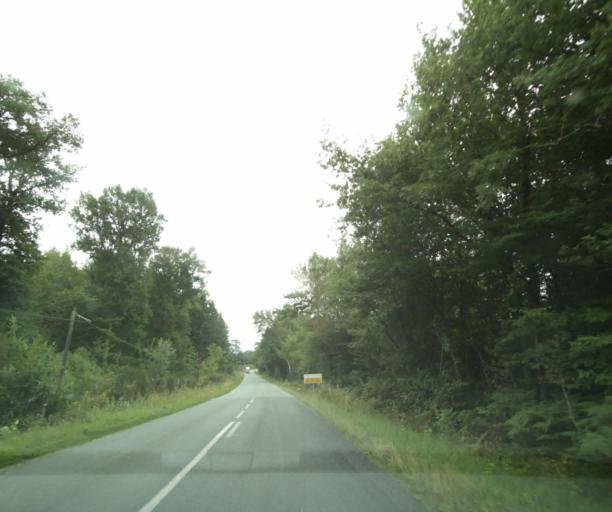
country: FR
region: Pays de la Loire
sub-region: Departement de Maine-et-Loire
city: Durtal
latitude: 47.7032
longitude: -0.2680
